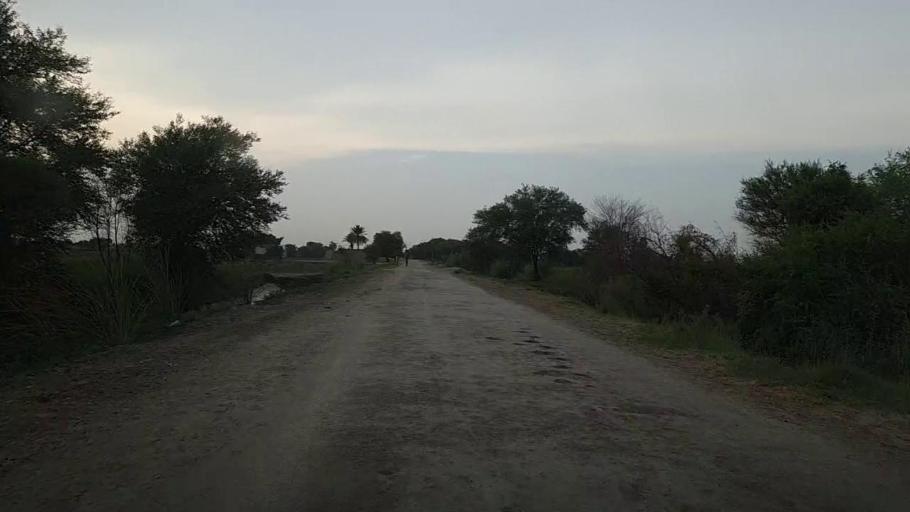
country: PK
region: Sindh
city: Khanpur
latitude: 27.8452
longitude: 69.4596
